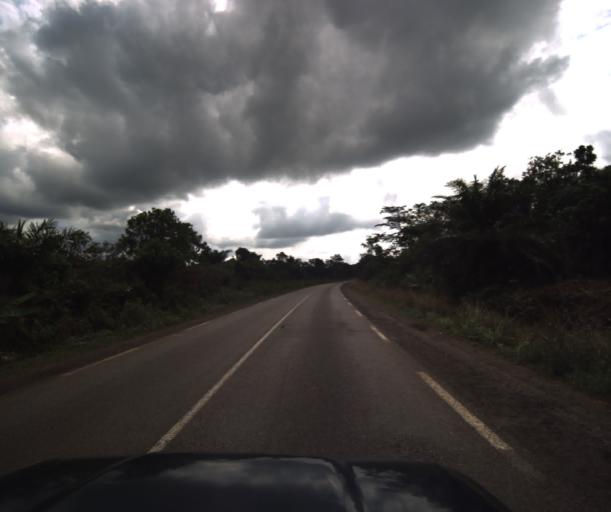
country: CM
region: Littoral
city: Edea
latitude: 3.8127
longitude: 10.3057
